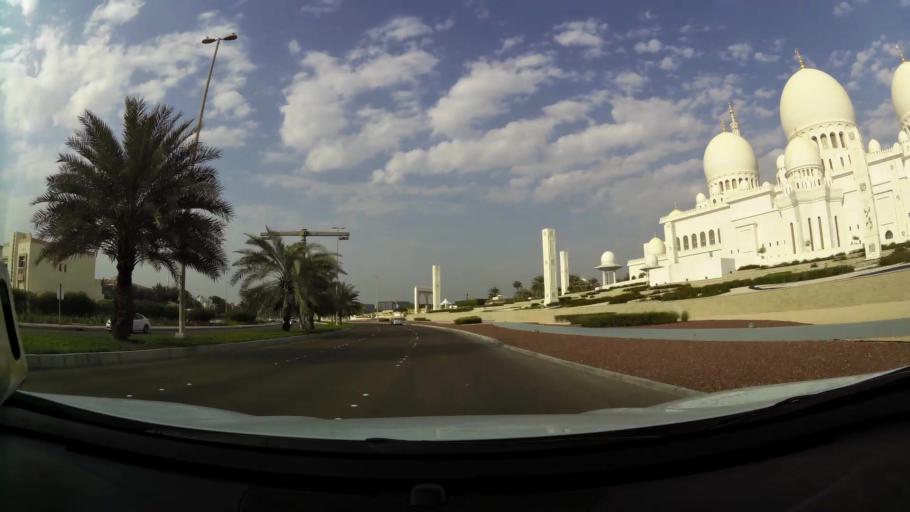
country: AE
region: Abu Dhabi
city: Abu Dhabi
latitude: 24.4121
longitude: 54.4727
